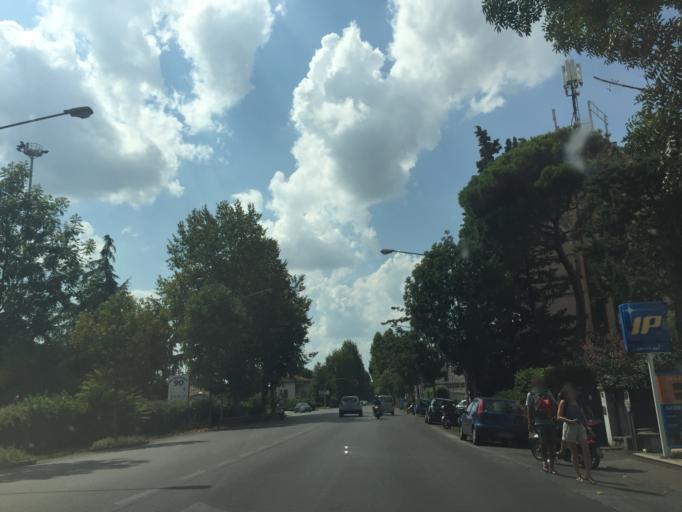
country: IT
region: Tuscany
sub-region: Province of Florence
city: Mantignano-Ugnano
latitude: 43.7954
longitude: 11.2005
